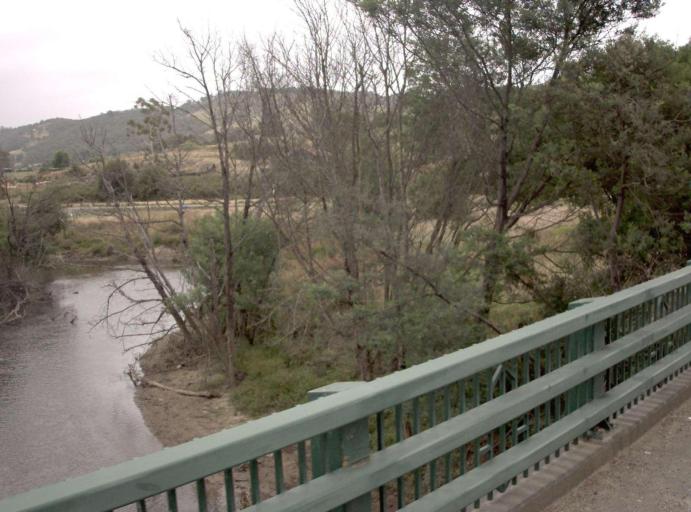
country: AU
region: Victoria
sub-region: Yarra Ranges
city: Yarra Glen
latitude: -37.6621
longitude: 145.3749
